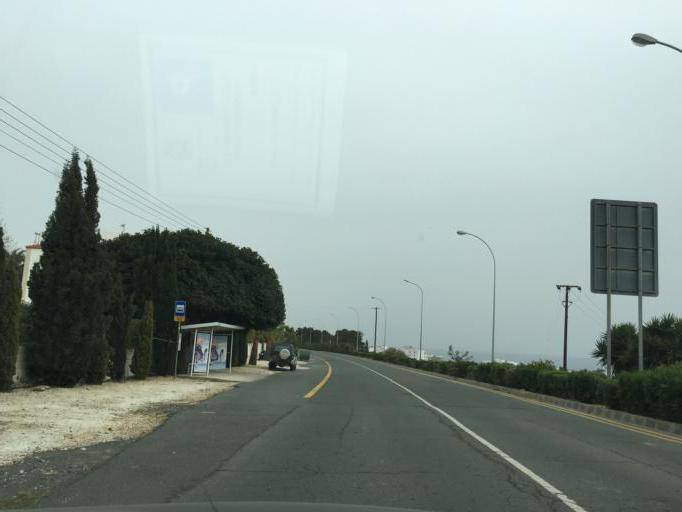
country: CY
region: Ammochostos
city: Ayia Napa
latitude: 34.9925
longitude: 34.0026
